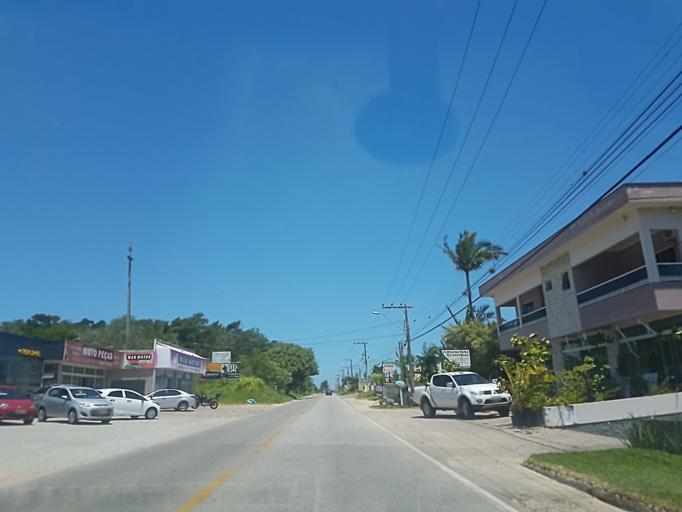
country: BR
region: Santa Catarina
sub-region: Jaguaruna
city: Jaguaruna
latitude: -28.6088
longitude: -49.0299
